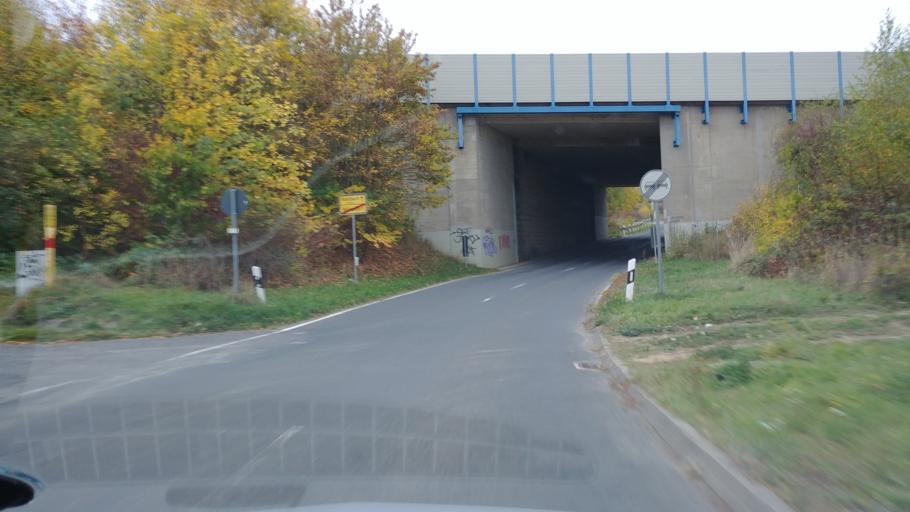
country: DE
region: Hesse
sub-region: Regierungsbezirk Darmstadt
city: Idstein
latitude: 50.2480
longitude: 8.2476
